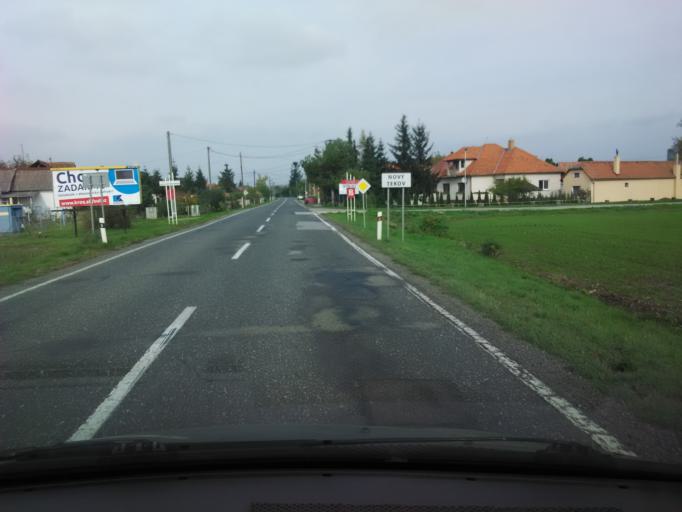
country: SK
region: Nitriansky
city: Tlmace
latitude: 48.2311
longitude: 18.5212
